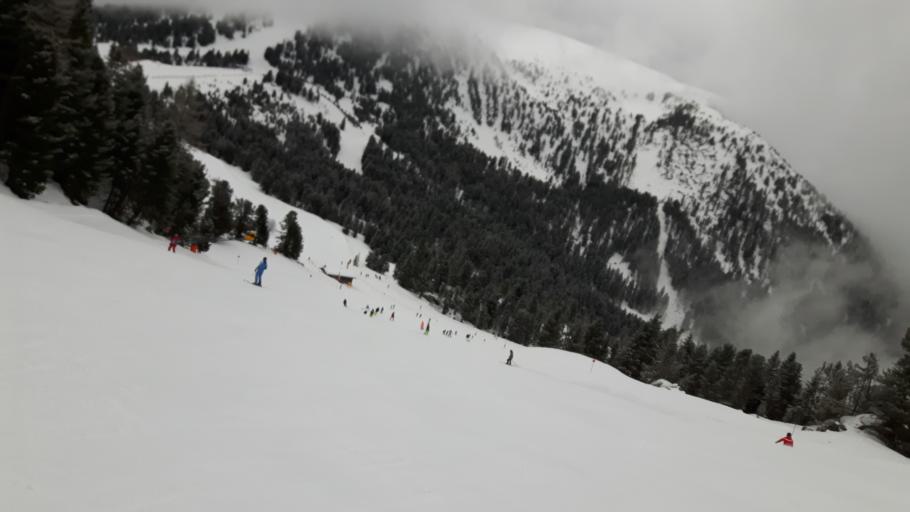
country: IT
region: Trentino-Alto Adige
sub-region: Bolzano
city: Nova Levante
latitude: 46.3601
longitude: 11.5432
